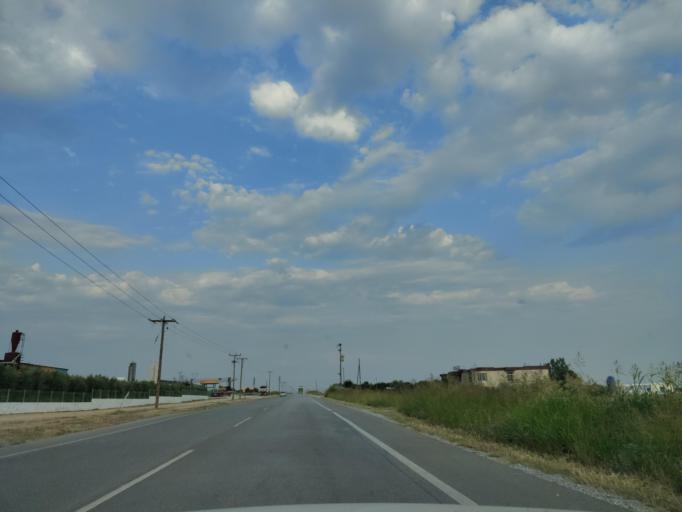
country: GR
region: East Macedonia and Thrace
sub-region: Nomos Dramas
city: Prosotsani
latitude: 41.1791
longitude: 23.9926
